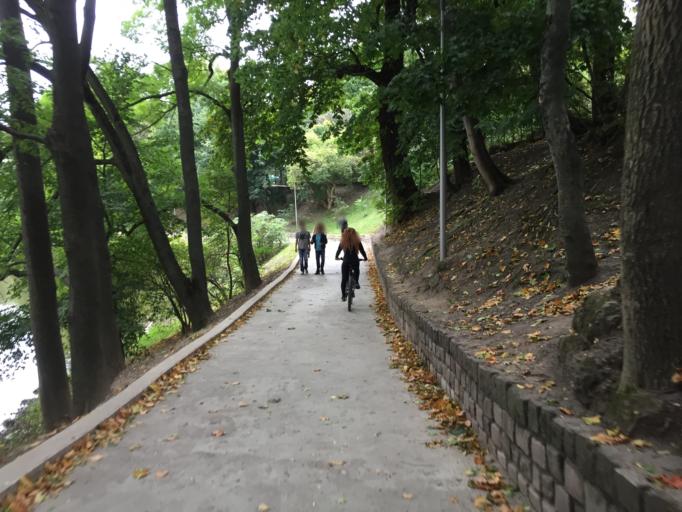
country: RU
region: Kaliningrad
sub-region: Gorod Kaliningrad
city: Kaliningrad
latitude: 54.7166
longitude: 20.5196
